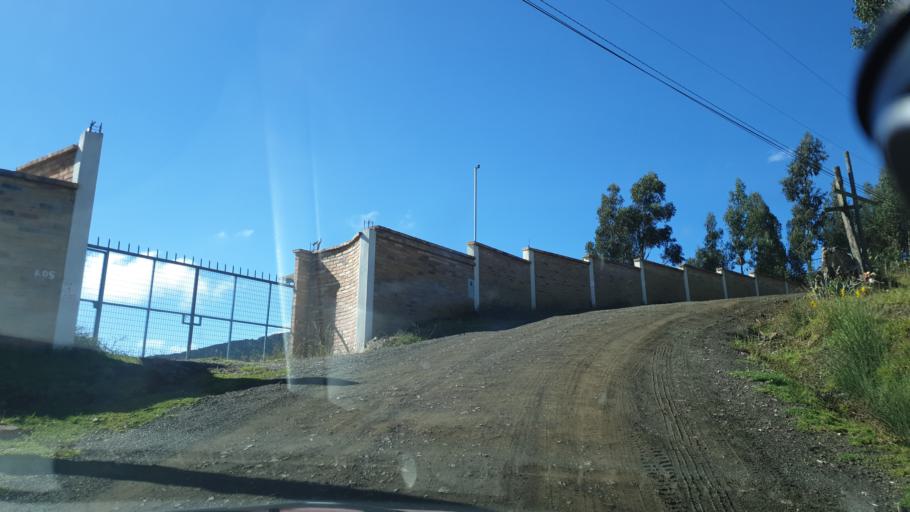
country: EC
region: Azuay
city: Llacao
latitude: -2.8648
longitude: -78.9124
